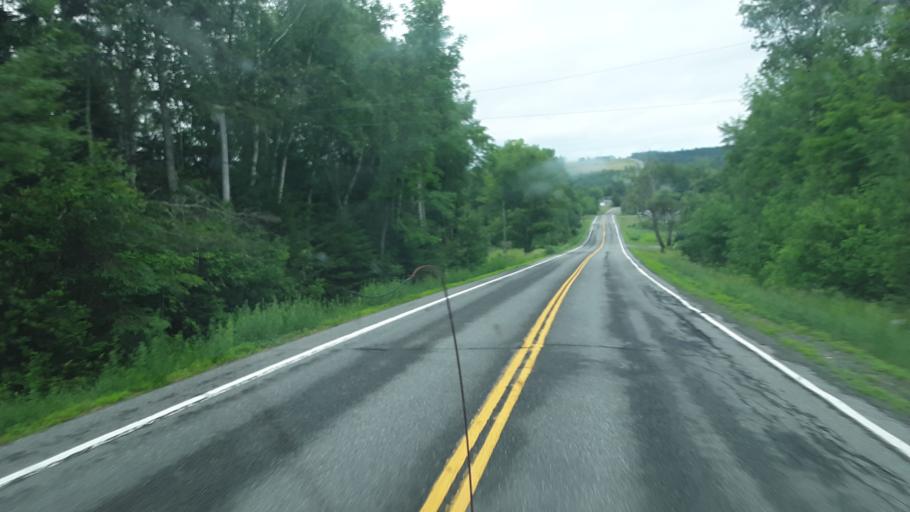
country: US
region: Maine
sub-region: Penobscot County
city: Patten
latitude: 46.0638
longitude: -68.4387
